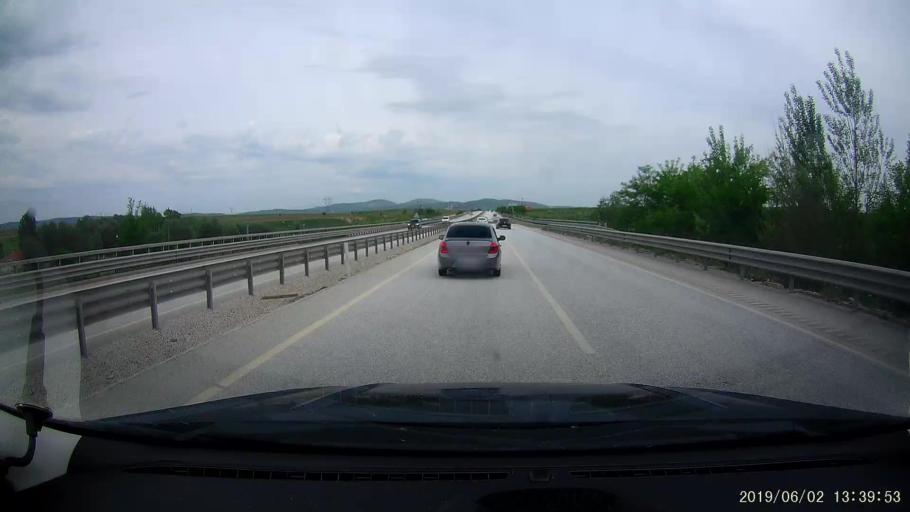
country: TR
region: Cankiri
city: Atkaracalar
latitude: 40.8312
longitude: 33.1402
